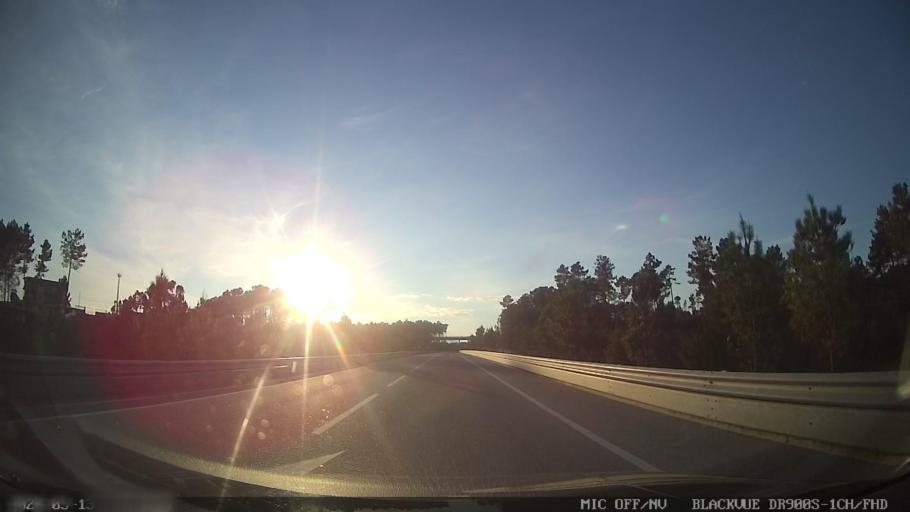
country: PT
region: Vila Real
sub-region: Vila Real
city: Vila Real
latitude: 41.2726
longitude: -7.6881
